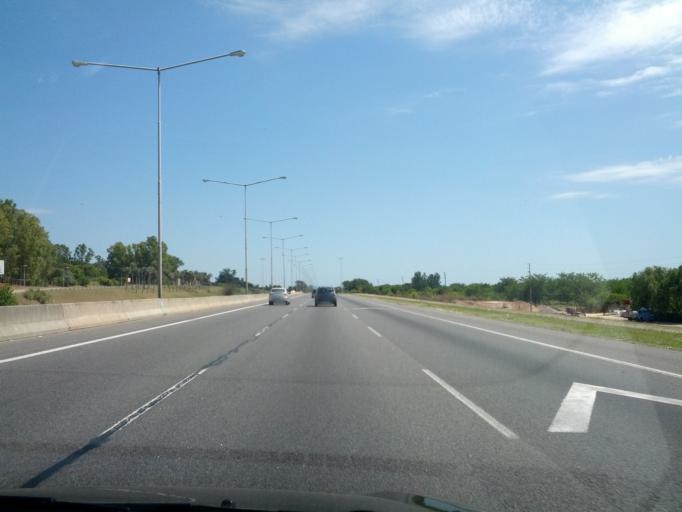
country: AR
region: Buenos Aires
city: Belen de Escobar
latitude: -34.2813
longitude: -58.8933
